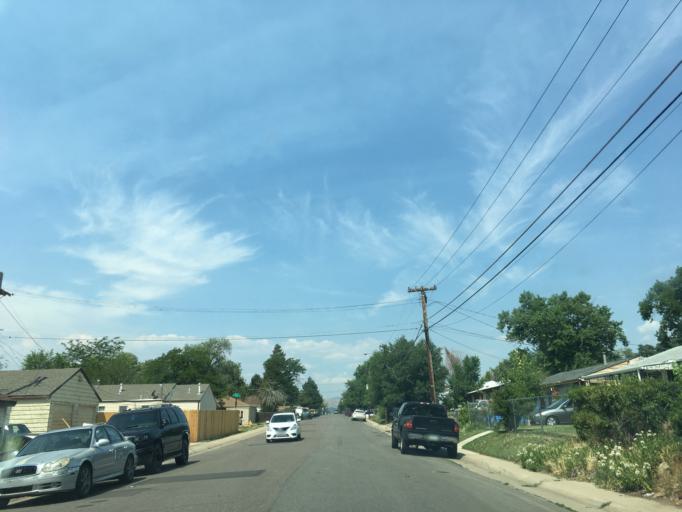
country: US
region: Colorado
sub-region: Jefferson County
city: Lakewood
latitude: 39.6968
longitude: -105.0451
